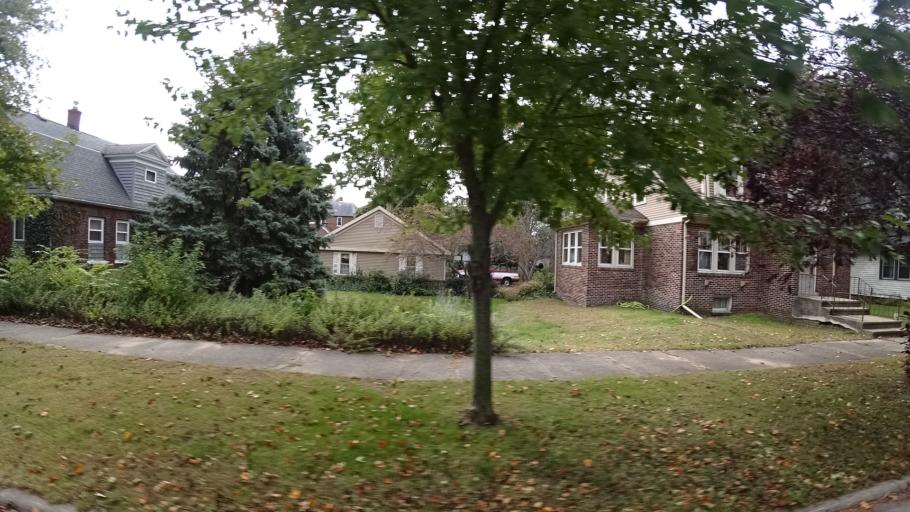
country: US
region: Indiana
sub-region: LaPorte County
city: Michigan City
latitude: 41.6994
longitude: -86.8929
